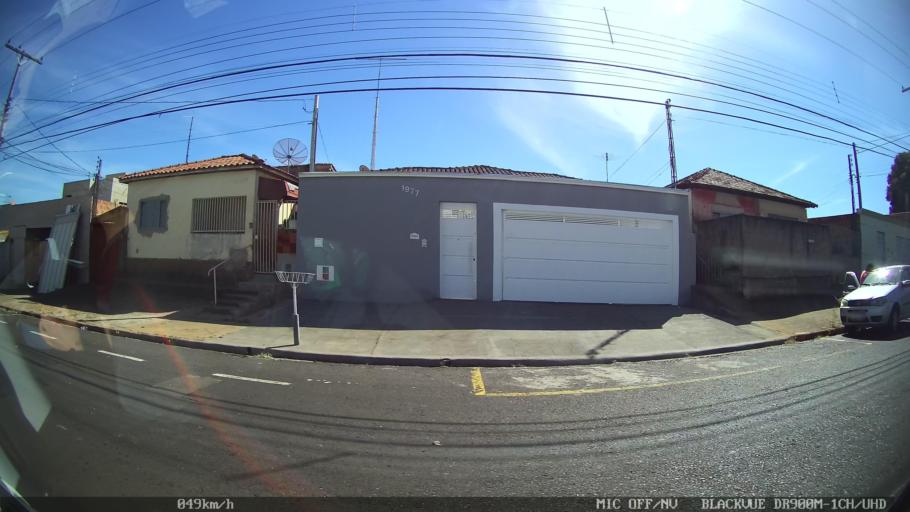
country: BR
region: Sao Paulo
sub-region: Franca
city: Franca
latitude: -20.5434
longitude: -47.3904
